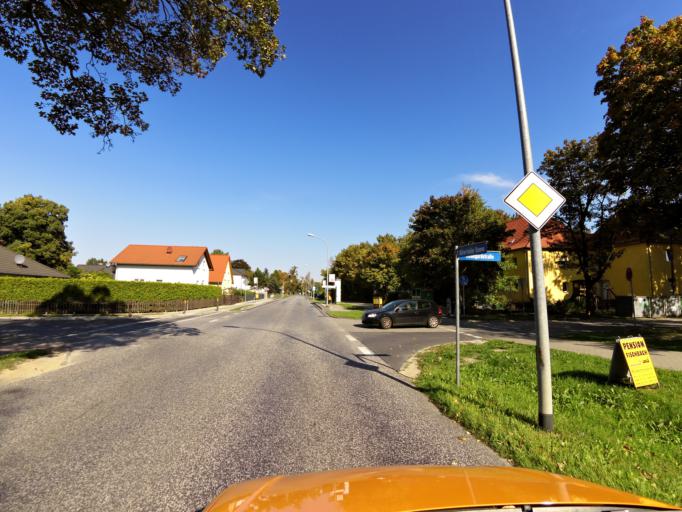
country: DE
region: Brandenburg
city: Stahnsdorf
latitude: 52.3785
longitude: 13.2080
